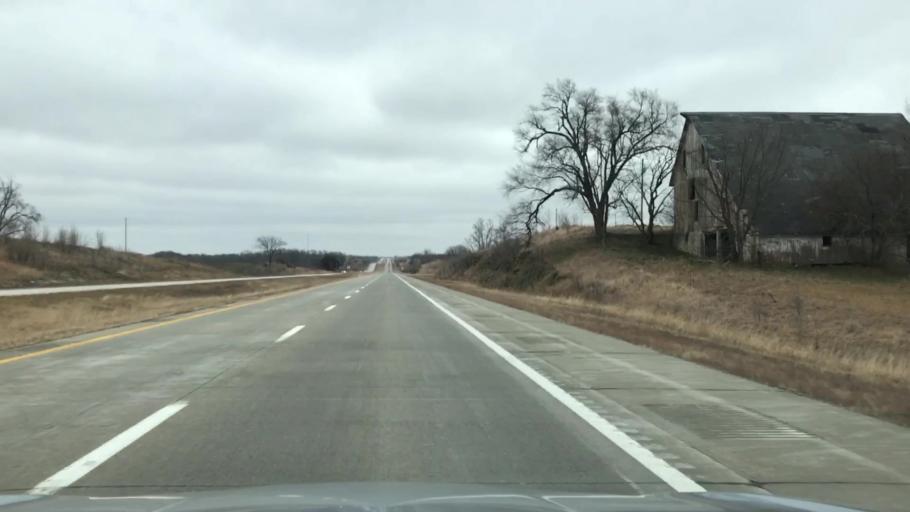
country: US
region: Missouri
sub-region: Caldwell County
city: Hamilton
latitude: 39.7350
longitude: -93.8361
